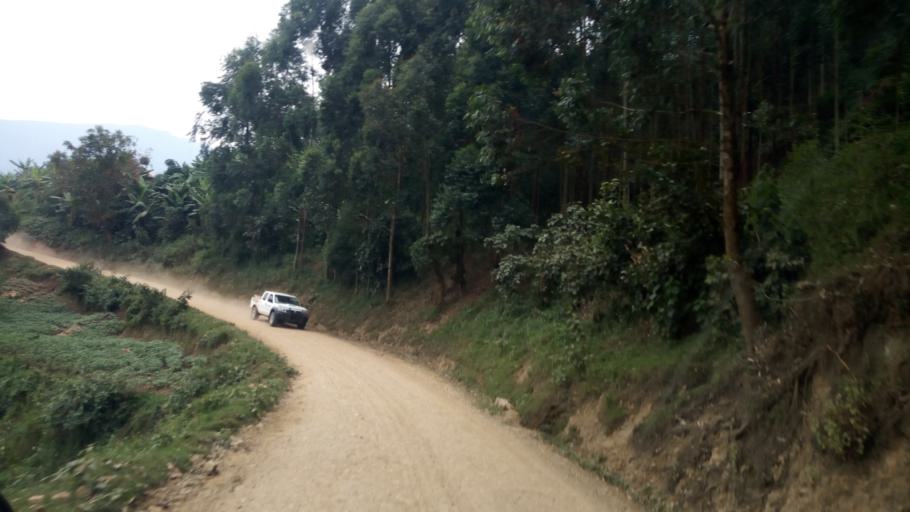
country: UG
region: Western Region
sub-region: Kanungu District
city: Kanungu
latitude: -1.1035
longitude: 29.8582
